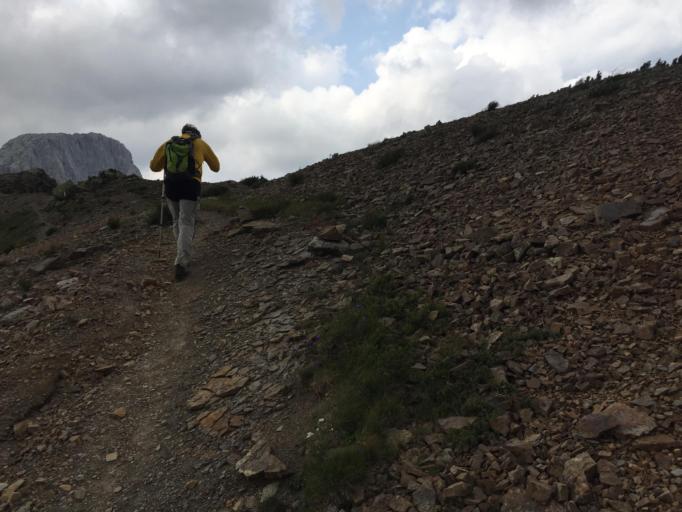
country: IT
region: Friuli Venezia Giulia
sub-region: Provincia di Udine
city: Pontebba
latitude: 46.5598
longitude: 13.2314
